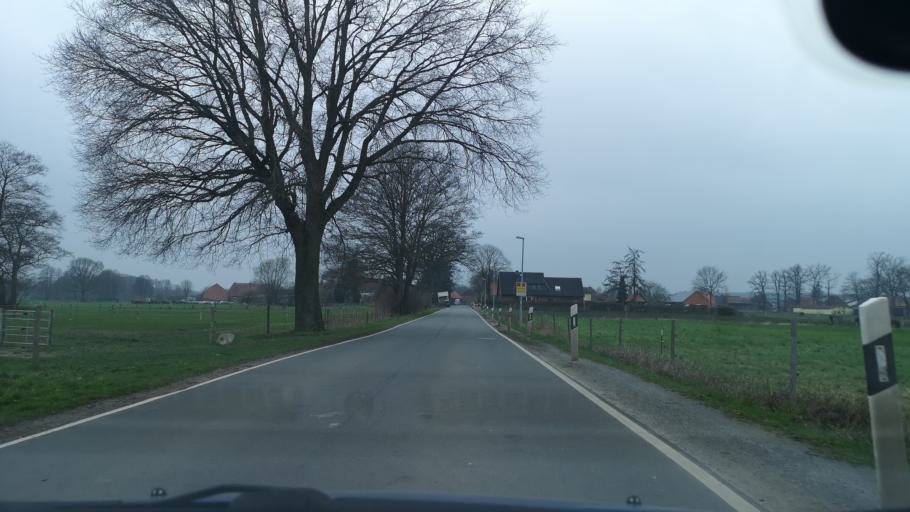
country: DE
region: Lower Saxony
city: Neustadt am Rubenberge
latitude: 52.5462
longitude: 9.4223
